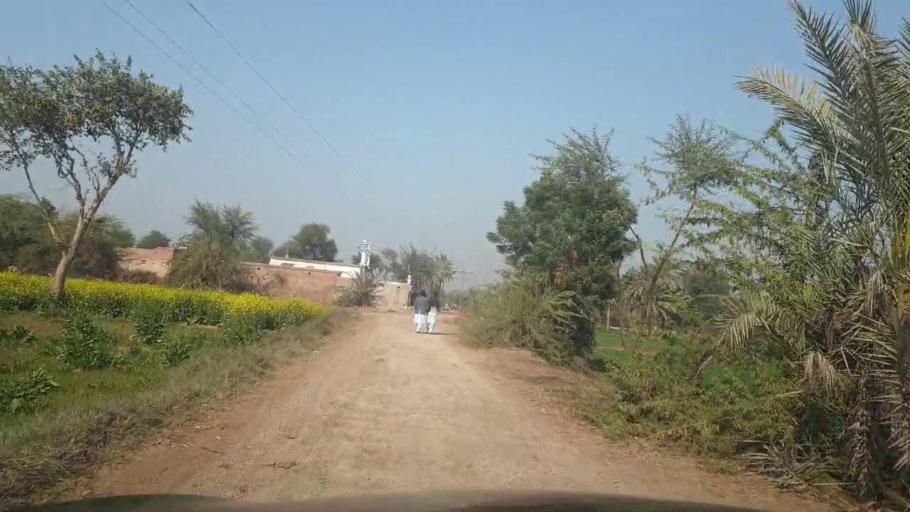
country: PK
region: Sindh
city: Ubauro
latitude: 28.0950
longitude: 69.8411
